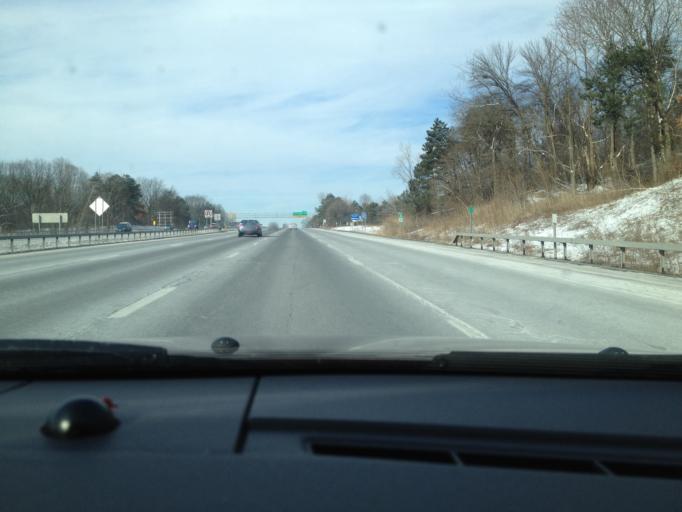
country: US
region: New York
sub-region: Albany County
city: Albany
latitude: 42.6727
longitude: -73.7567
